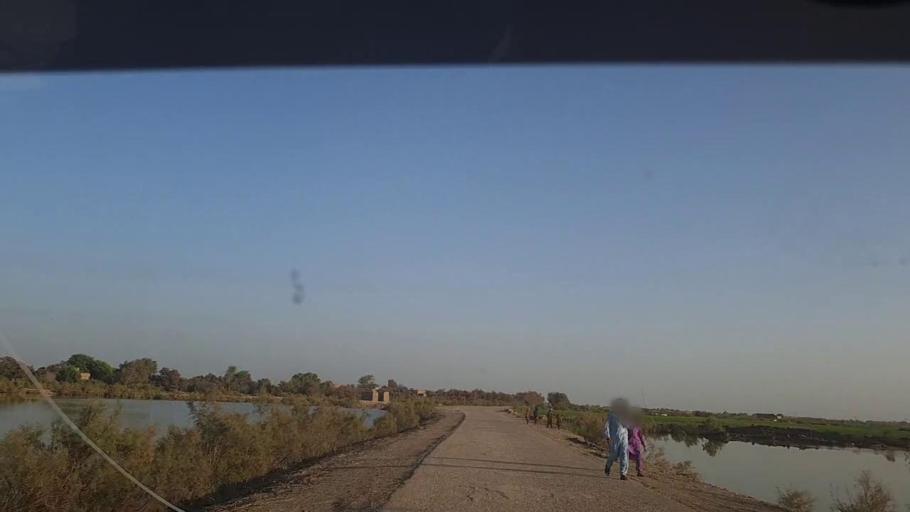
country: PK
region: Sindh
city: Thul
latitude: 28.1484
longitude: 68.8873
